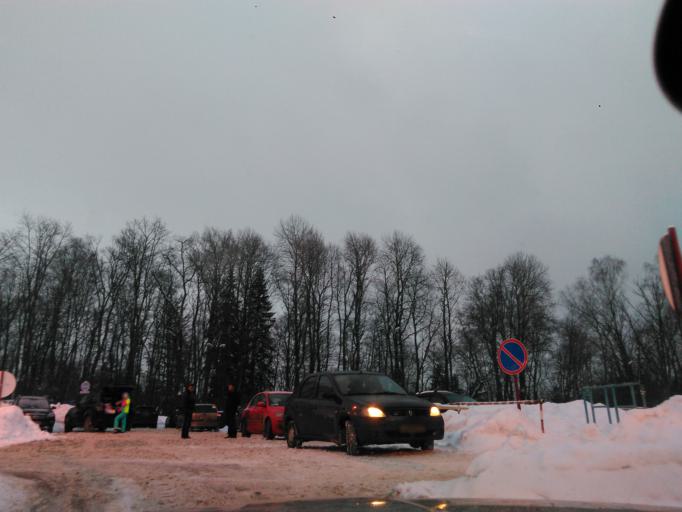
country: RU
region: Moskovskaya
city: Yakhroma
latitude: 56.2601
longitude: 37.4298
